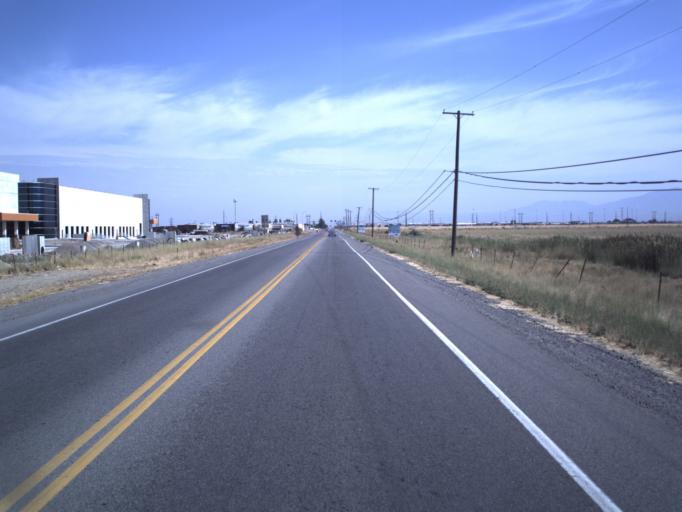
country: US
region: Utah
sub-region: Salt Lake County
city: West Valley City
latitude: 40.7349
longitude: -112.0249
